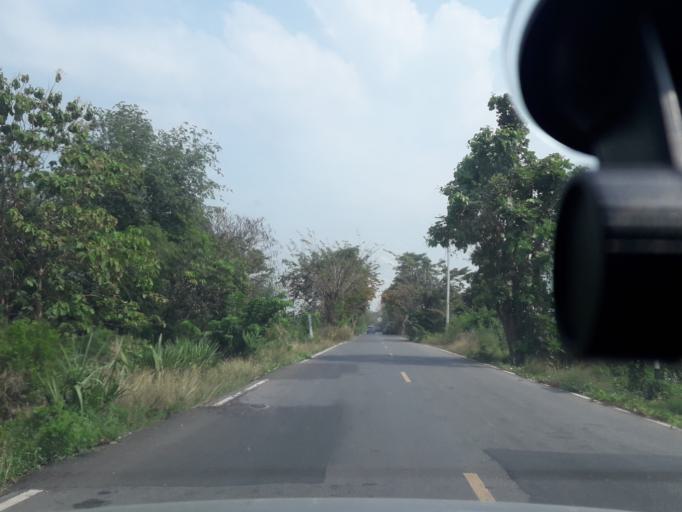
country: TH
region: Pathum Thani
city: Nong Suea
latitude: 14.1968
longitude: 100.8791
